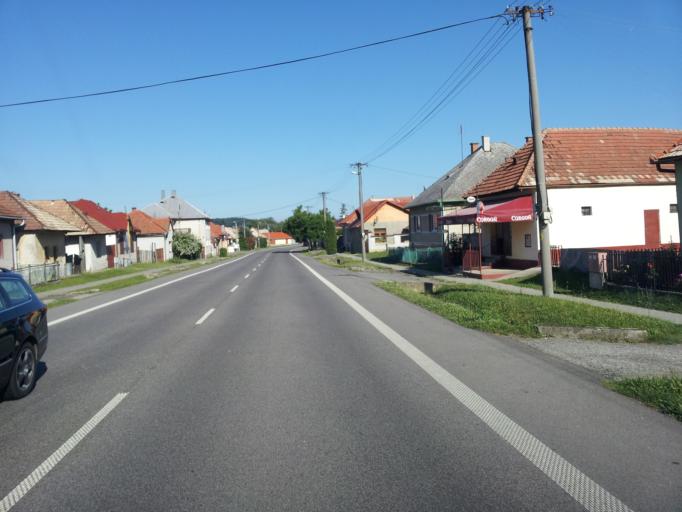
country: SK
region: Nitriansky
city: Sahy
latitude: 48.0885
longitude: 18.9010
